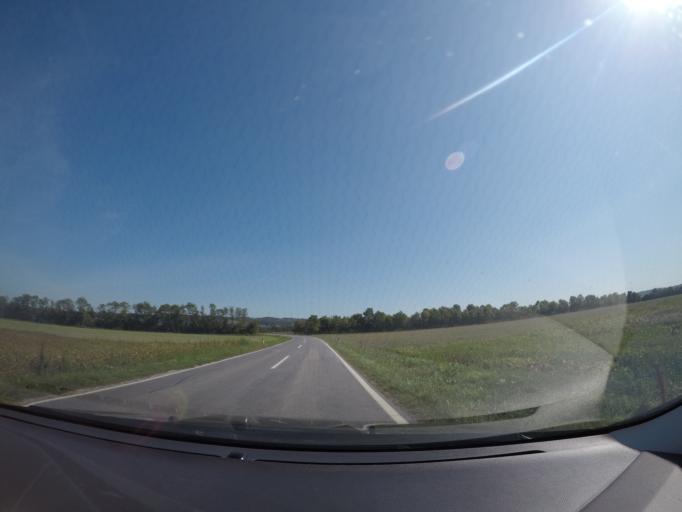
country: AT
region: Lower Austria
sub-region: Politischer Bezirk Bruck an der Leitha
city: Au am Leithaberge
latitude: 47.9462
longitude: 16.5559
